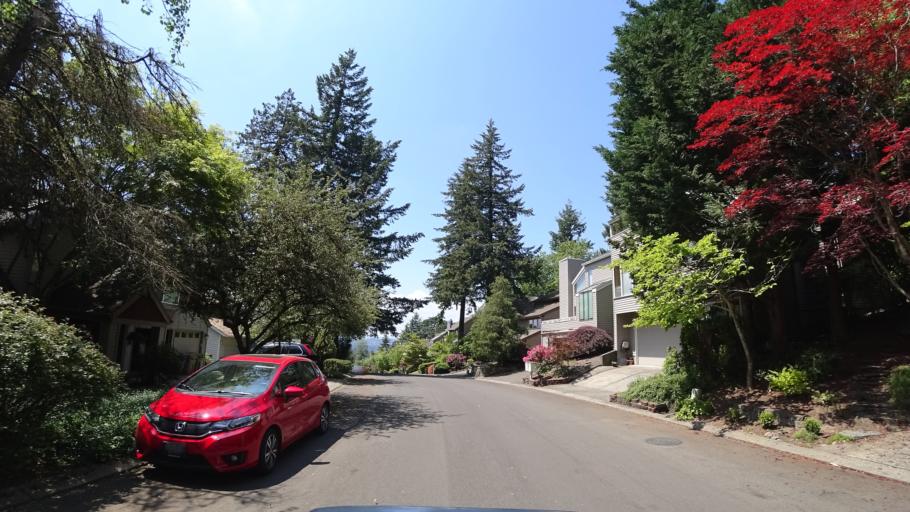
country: US
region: Oregon
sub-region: Washington County
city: Metzger
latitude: 45.4337
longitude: -122.7270
